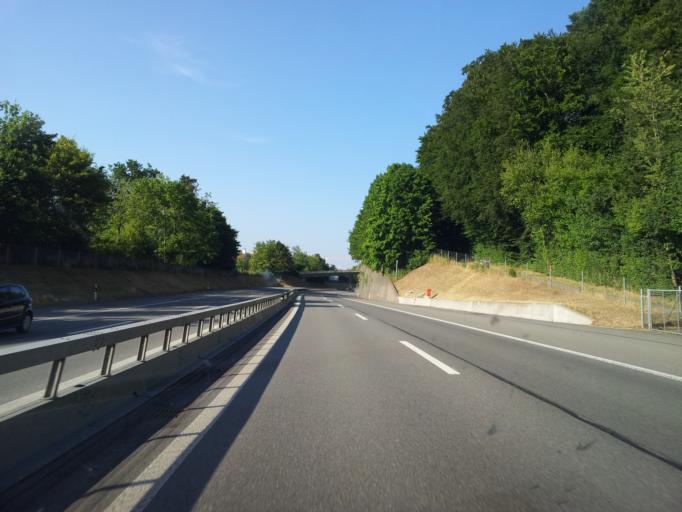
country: CH
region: Bern
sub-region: Bern-Mittelland District
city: Koniz
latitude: 46.9349
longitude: 7.3966
